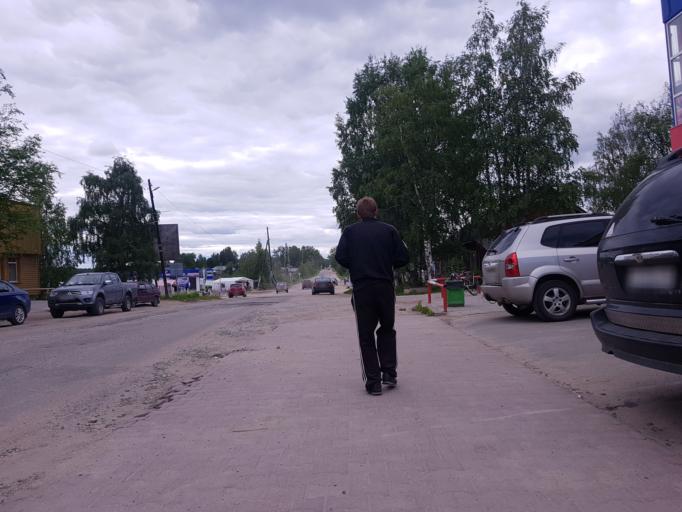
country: RU
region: Republic of Karelia
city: Kalevala
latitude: 65.1977
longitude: 31.1807
